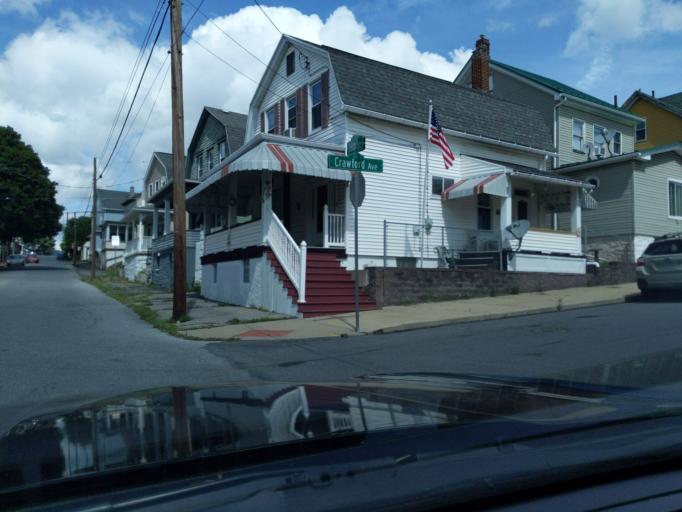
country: US
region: Pennsylvania
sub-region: Blair County
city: Altoona
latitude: 40.5053
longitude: -78.3946
